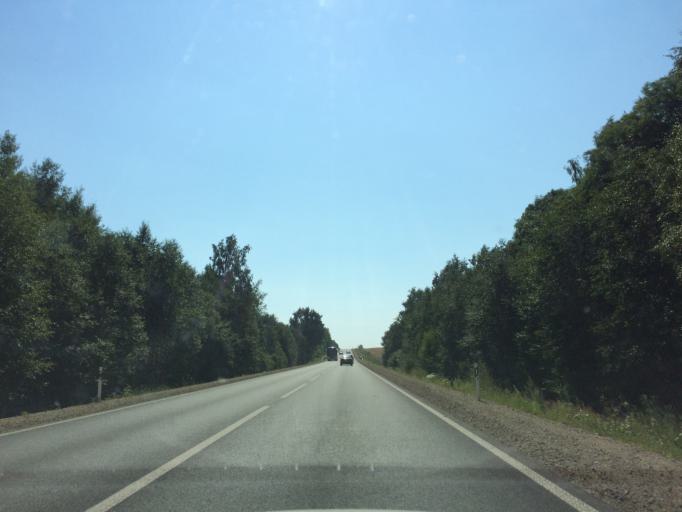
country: LV
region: Rezekne
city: Rezekne
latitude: 56.3855
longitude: 27.2058
